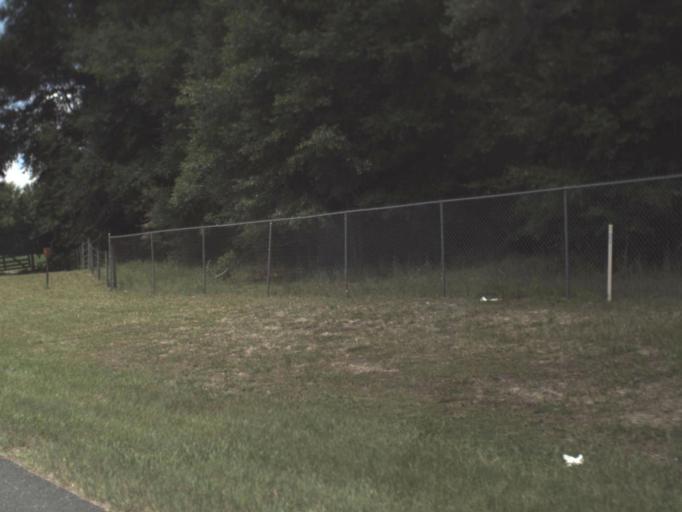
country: US
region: Florida
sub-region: Gilchrist County
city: Trenton
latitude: 29.7709
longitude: -82.8666
